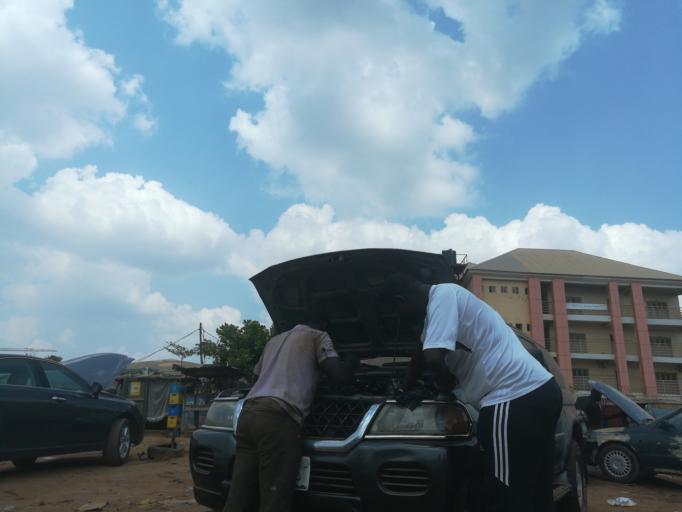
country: NG
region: Abuja Federal Capital Territory
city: Abuja
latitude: 9.0594
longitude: 7.4479
